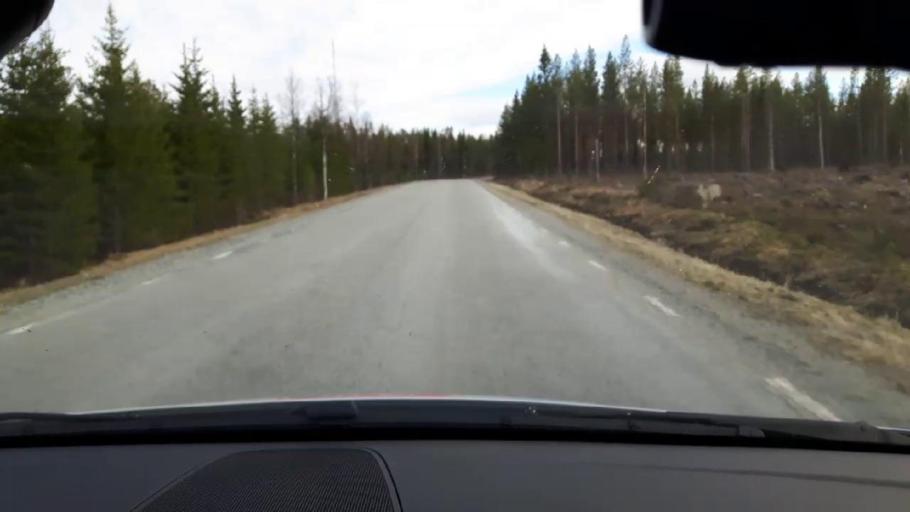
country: SE
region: Jaemtland
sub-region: Bergs Kommun
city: Hoverberg
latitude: 62.7060
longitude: 14.6172
